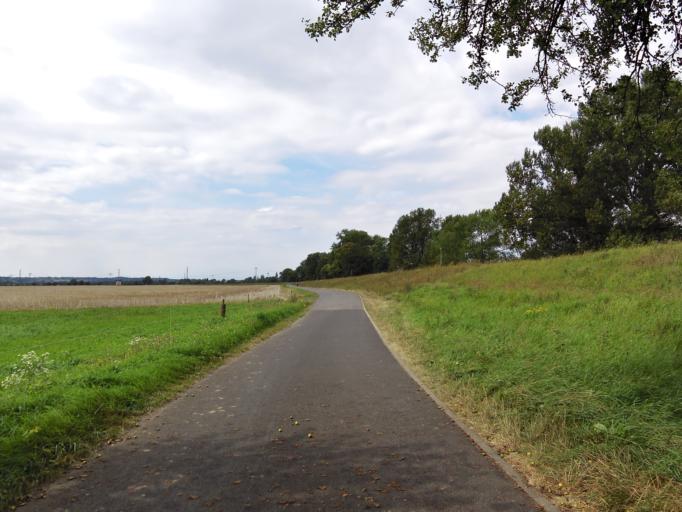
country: DE
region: Saxony
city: Radebeul
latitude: 51.0970
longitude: 13.6354
